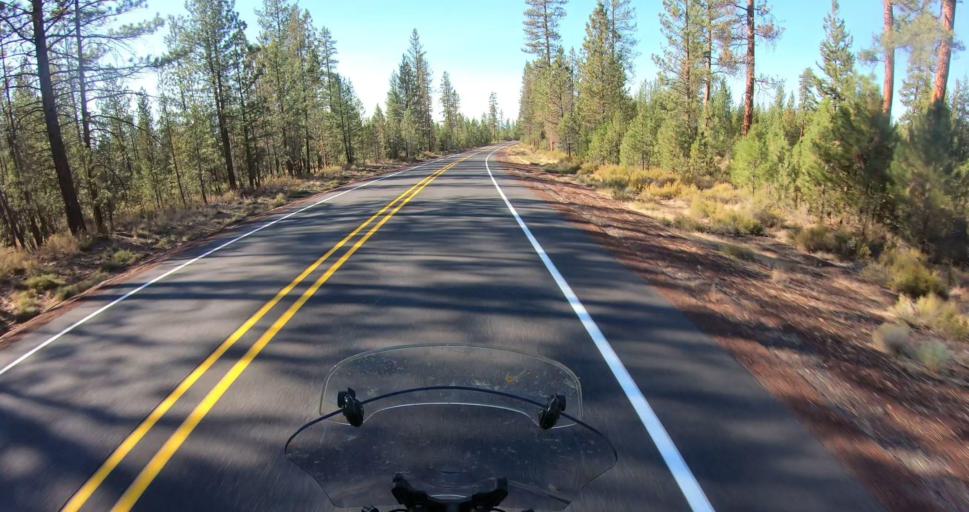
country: US
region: Oregon
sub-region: Deschutes County
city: La Pine
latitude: 43.4934
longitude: -121.4433
